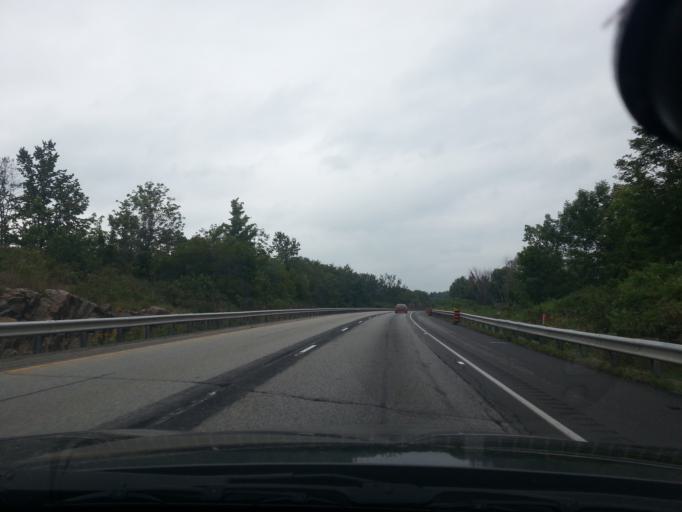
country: US
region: New York
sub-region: Jefferson County
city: Alexandria Bay
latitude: 44.3970
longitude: -75.9498
